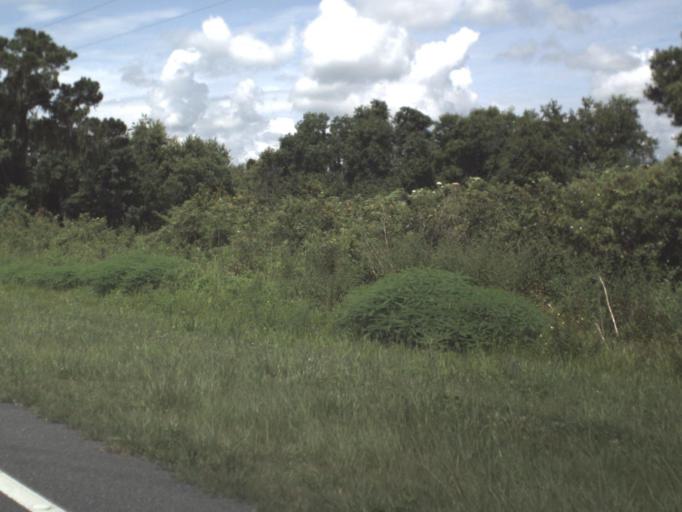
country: US
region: Florida
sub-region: Alachua County
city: Alachua
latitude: 29.8353
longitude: -82.4111
